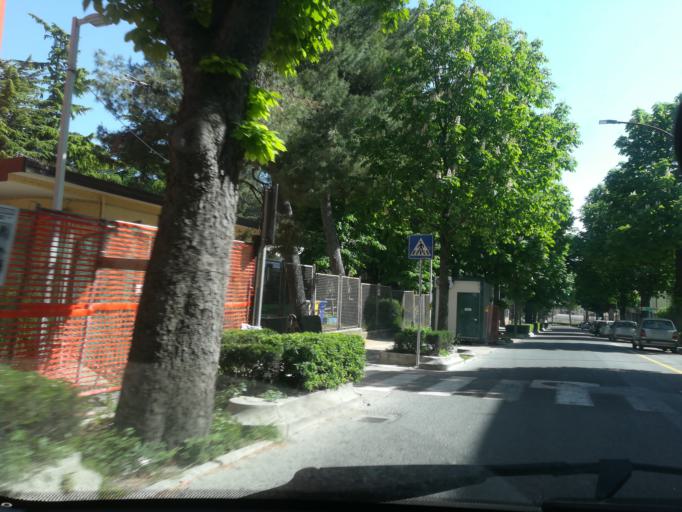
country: IT
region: The Marches
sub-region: Provincia di Macerata
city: Macerata
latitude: 43.2960
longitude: 13.4538
